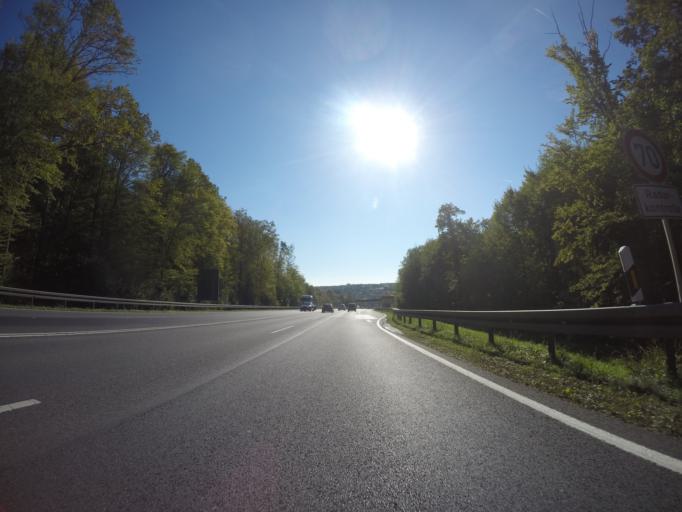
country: DE
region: Bavaria
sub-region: Regierungsbezirk Unterfranken
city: Hochberg
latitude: 49.7891
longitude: 9.8739
